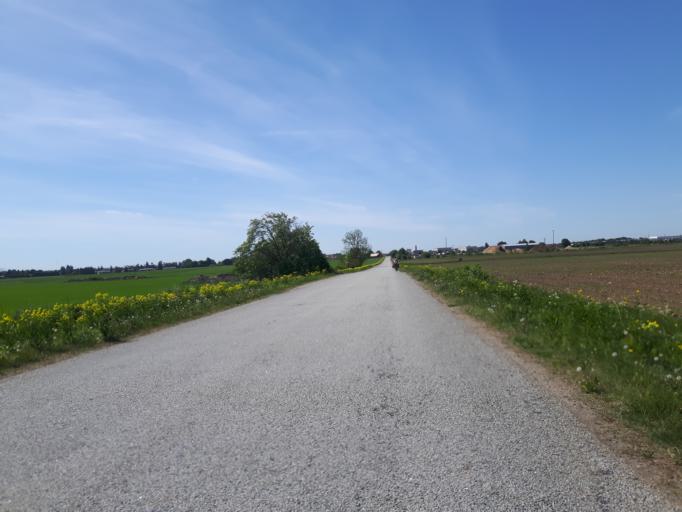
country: EE
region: Ida-Virumaa
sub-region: Aseri vald
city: Aseri
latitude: 59.4548
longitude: 26.7046
